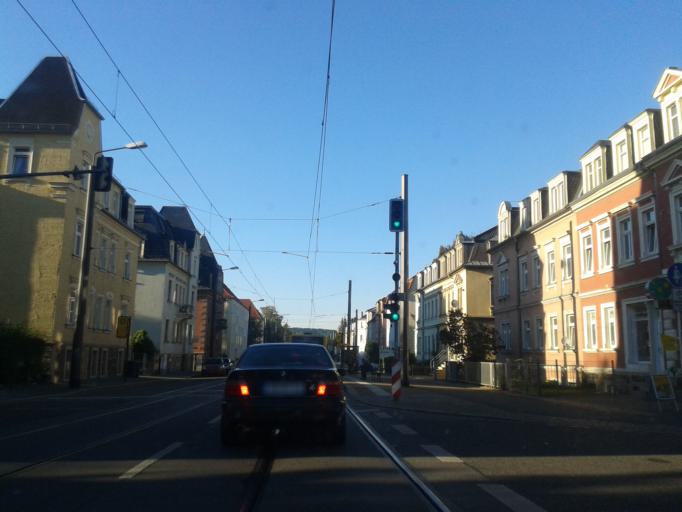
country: DE
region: Saxony
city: Dresden
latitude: 51.0858
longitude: 13.7048
